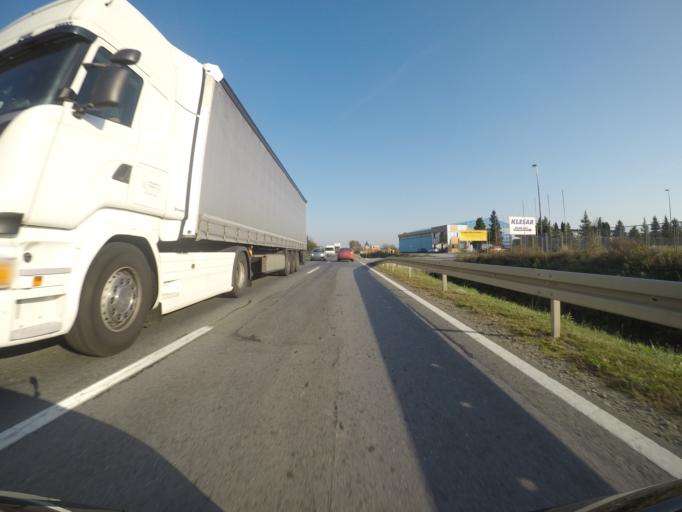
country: HR
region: Virovitick-Podravska
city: Pitomaca
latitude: 45.9667
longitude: 17.2037
